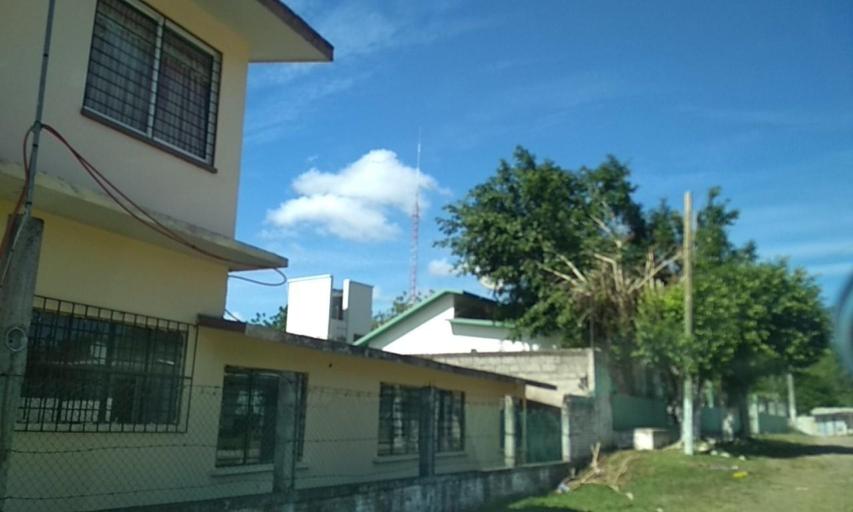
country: MX
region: Veracruz
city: Cazones de Herrera
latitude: 20.6446
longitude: -97.3051
